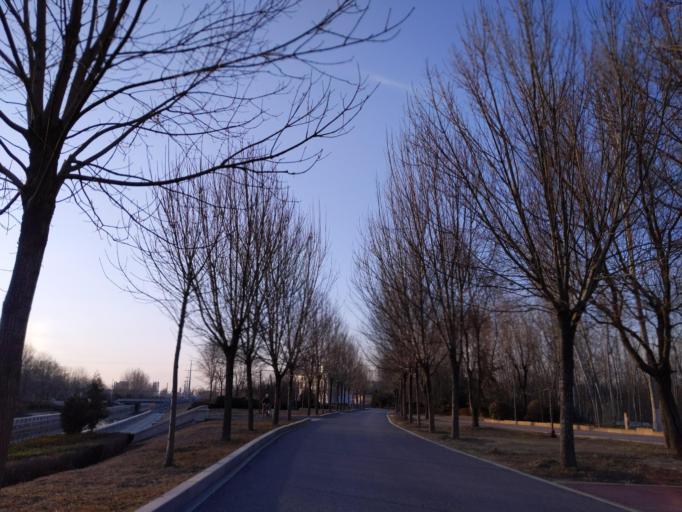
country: CN
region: Henan Sheng
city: Puyang
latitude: 35.7703
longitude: 114.9970
